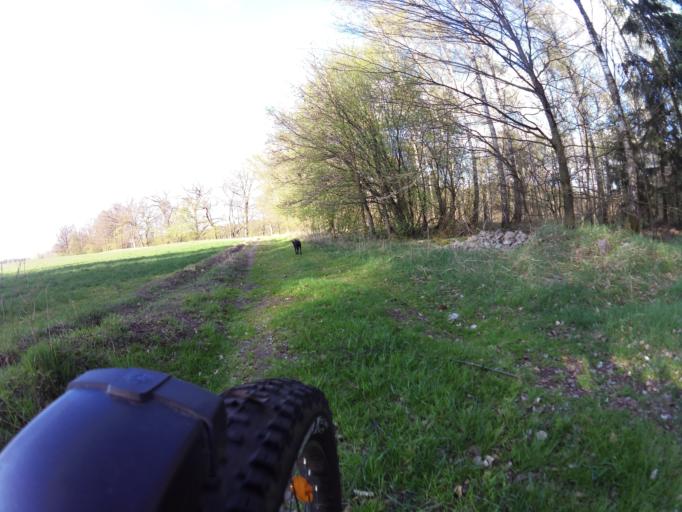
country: PL
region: West Pomeranian Voivodeship
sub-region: Powiat gryficki
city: Ploty
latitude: 53.7632
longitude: 15.2652
